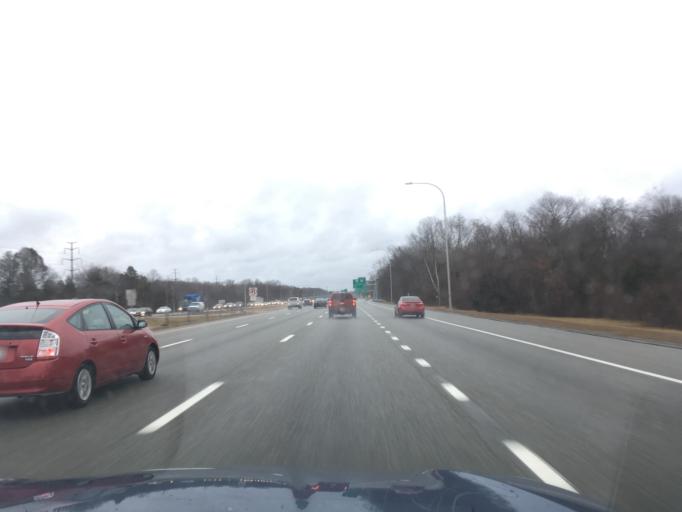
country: US
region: Rhode Island
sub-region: Kent County
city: East Greenwich
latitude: 41.6385
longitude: -71.4875
